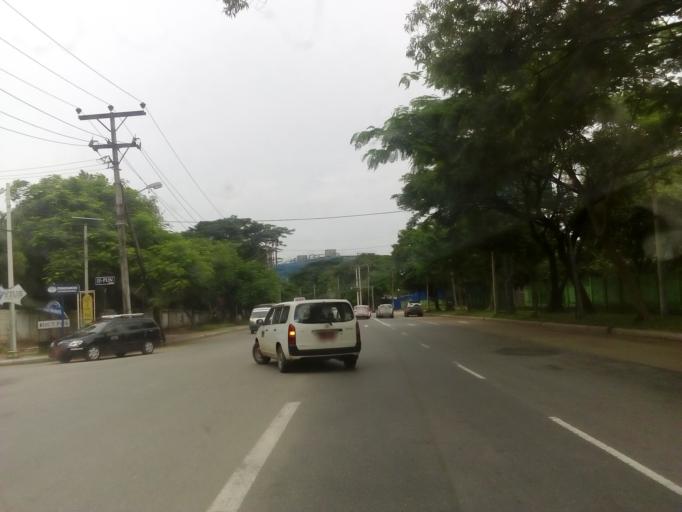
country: MM
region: Yangon
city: Yangon
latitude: 16.8571
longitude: 96.1307
